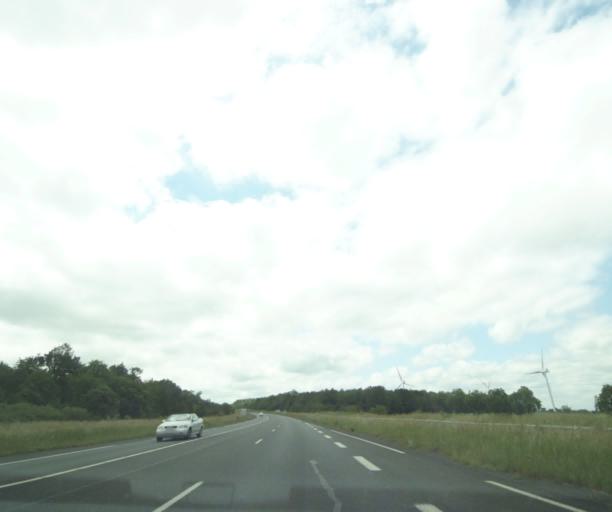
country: FR
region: Poitou-Charentes
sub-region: Departement des Deux-Sevres
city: Saint-Varent
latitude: 46.8656
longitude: -0.2066
